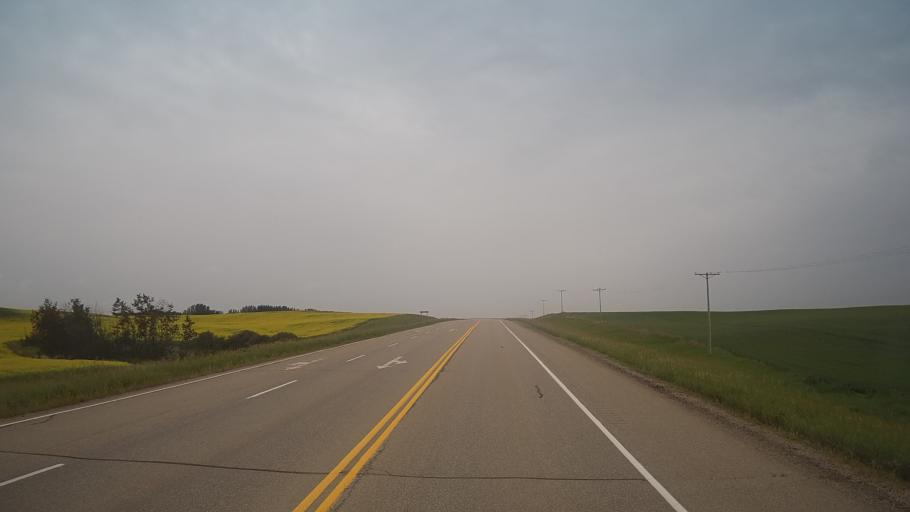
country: CA
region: Saskatchewan
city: Biggar
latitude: 52.0565
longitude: -107.7891
